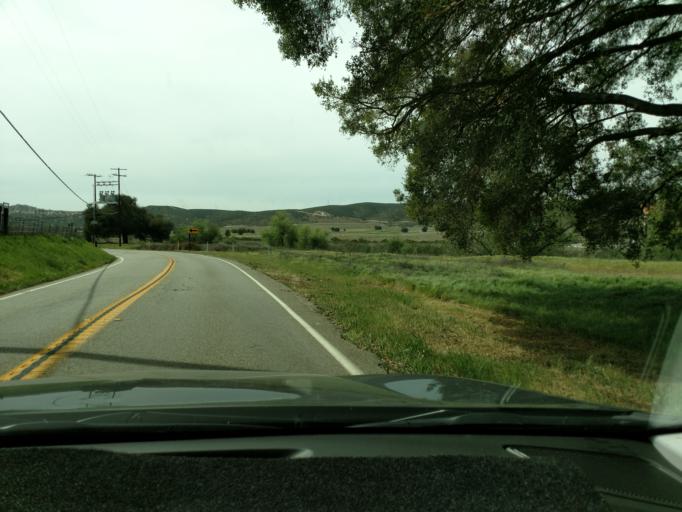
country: US
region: California
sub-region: San Diego County
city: Ramona
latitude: 32.9424
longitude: -116.8601
